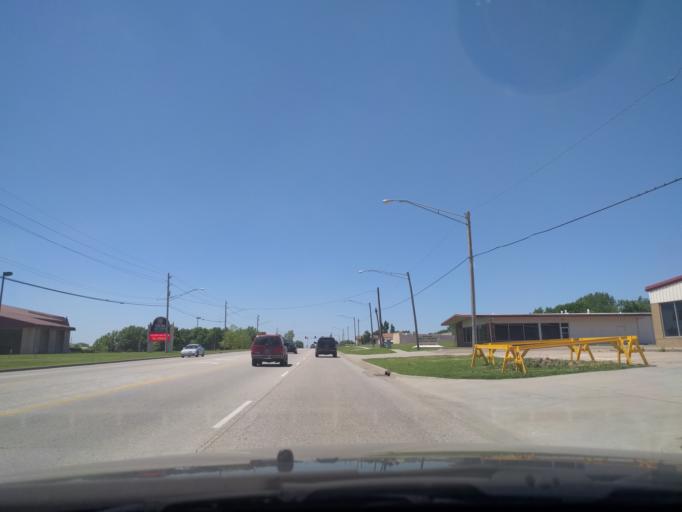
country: US
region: Oklahoma
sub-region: Tulsa County
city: Broken Arrow
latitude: 36.0610
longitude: -95.8021
